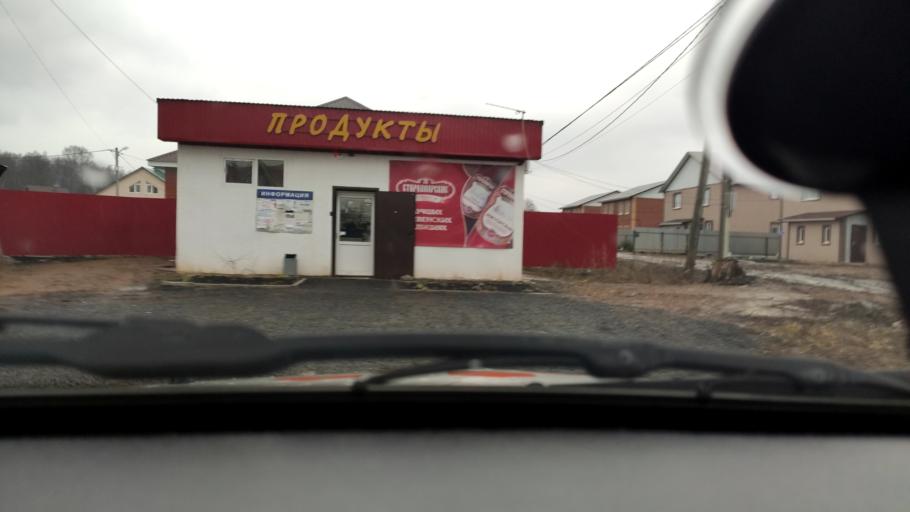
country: RU
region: Bashkortostan
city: Mikhaylovka
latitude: 54.7848
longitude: 55.8154
